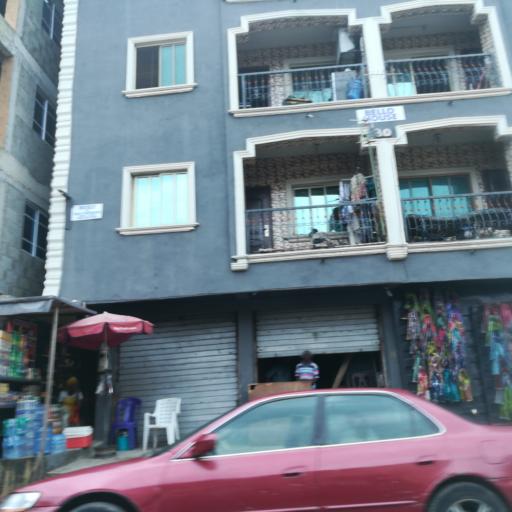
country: NG
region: Lagos
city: Ebute Metta
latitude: 6.4887
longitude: 3.3829
